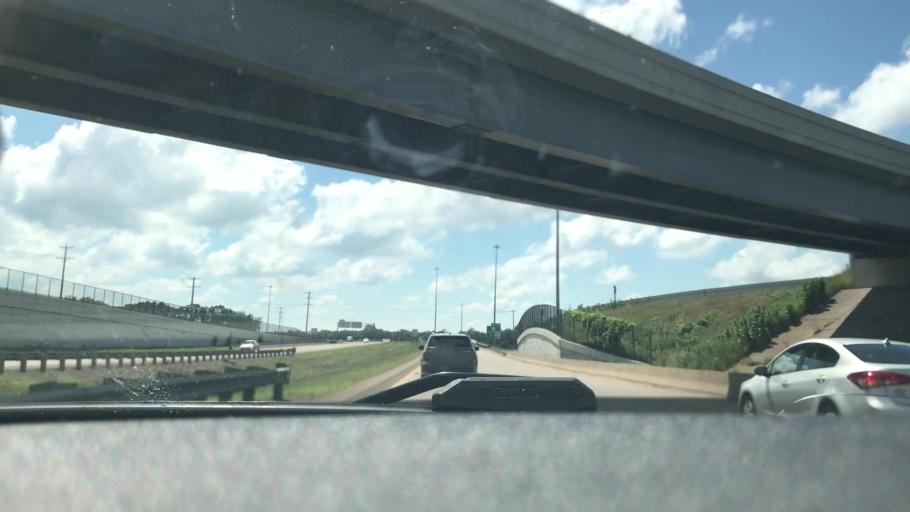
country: US
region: Wisconsin
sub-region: Eau Claire County
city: Altoona
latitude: 44.7899
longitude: -91.4542
